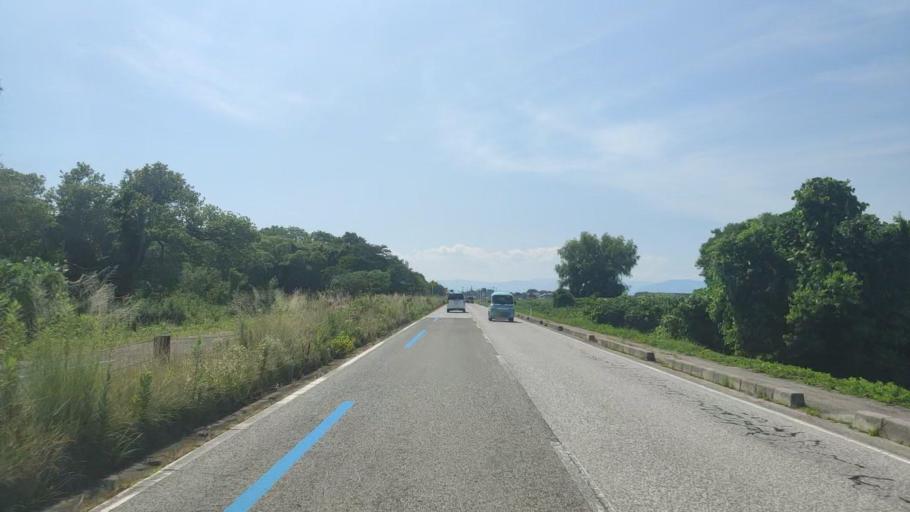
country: JP
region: Shiga Prefecture
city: Nagahama
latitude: 35.3881
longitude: 136.2306
